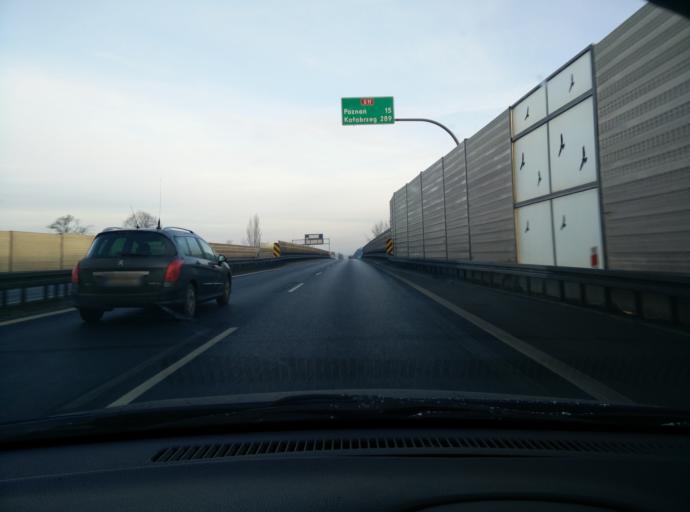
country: PL
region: Greater Poland Voivodeship
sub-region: Powiat poznanski
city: Kornik
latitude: 52.3000
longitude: 17.0492
